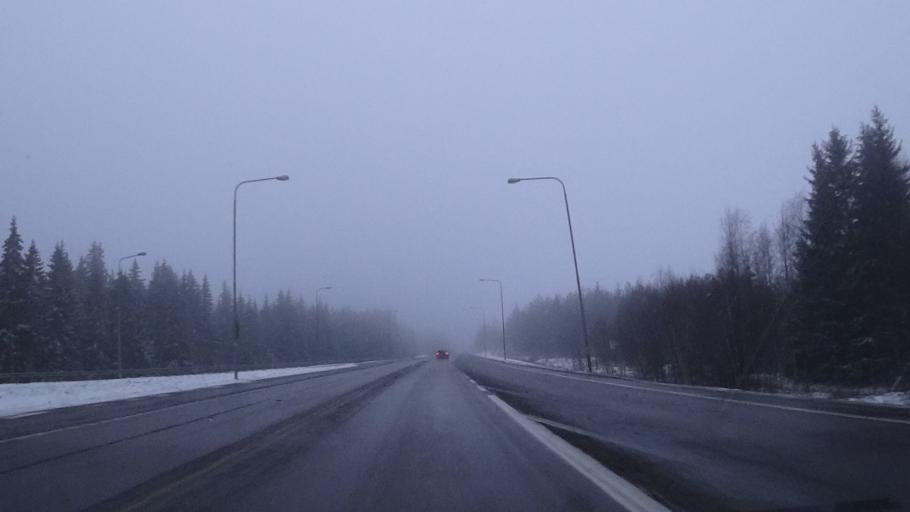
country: FI
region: Paijanne Tavastia
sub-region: Lahti
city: Hollola
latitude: 60.9841
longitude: 25.4144
